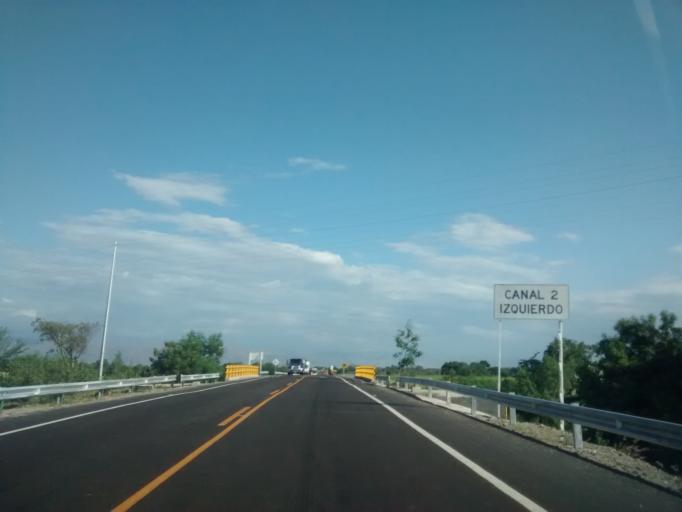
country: CO
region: Tolima
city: Espinal
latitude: 4.1537
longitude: -74.9152
